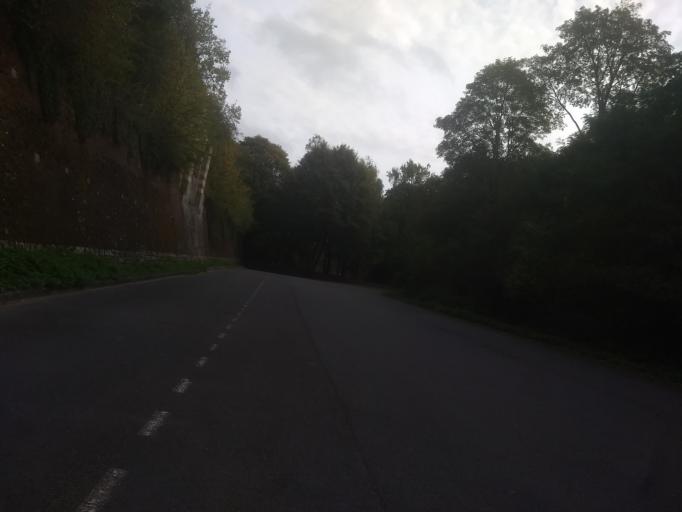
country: FR
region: Nord-Pas-de-Calais
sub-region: Departement du Pas-de-Calais
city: Achicourt
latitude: 50.2825
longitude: 2.7559
